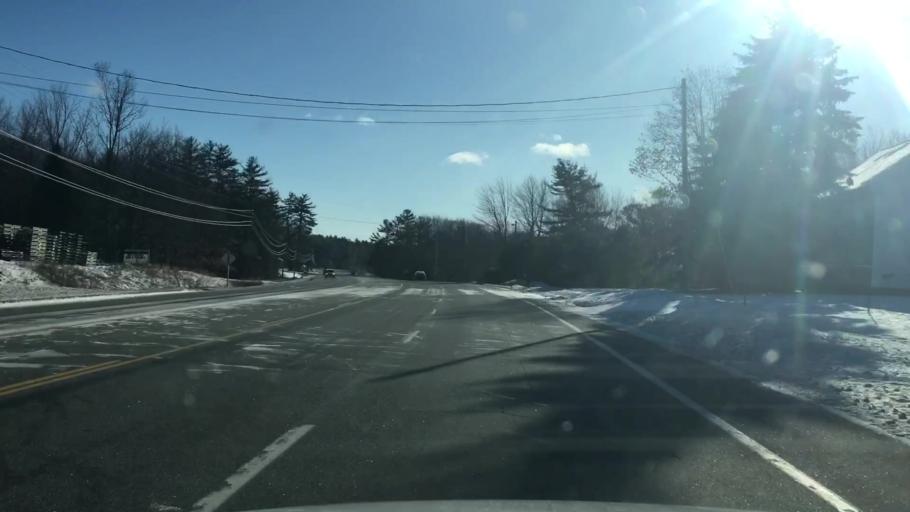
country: US
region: Maine
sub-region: Androscoggin County
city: Auburn
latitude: 44.1603
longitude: -70.2340
